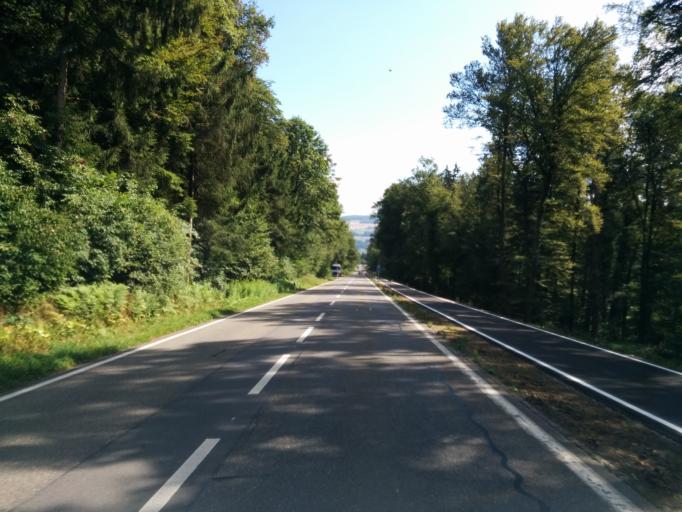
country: CH
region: Aargau
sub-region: Bezirk Muri
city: Waltenschwil
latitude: 47.3491
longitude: 8.3018
